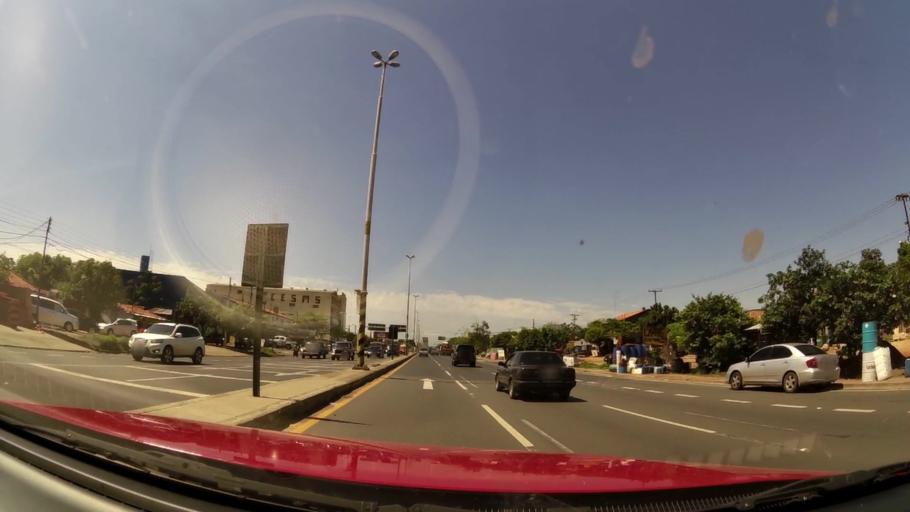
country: PY
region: Central
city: Colonia Mariano Roque Alonso
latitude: -25.2451
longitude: -57.5478
